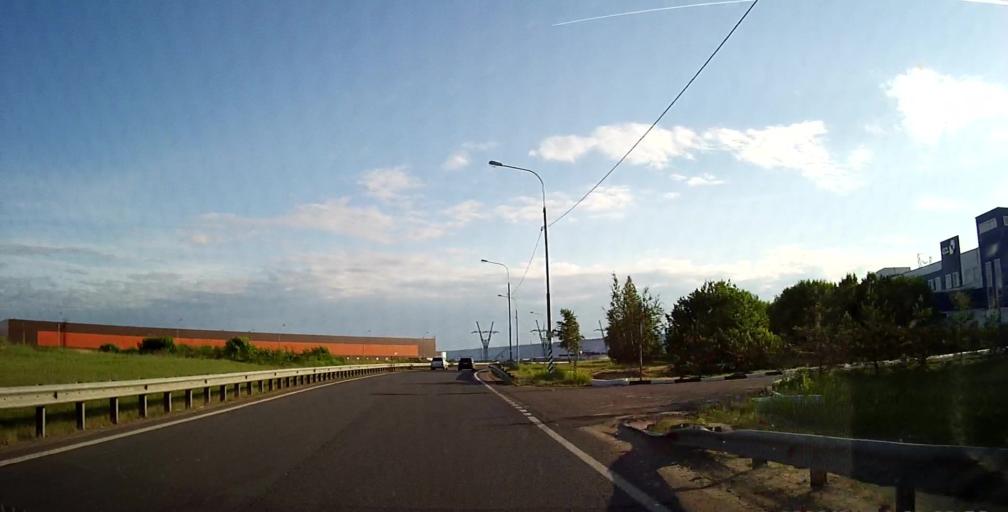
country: RU
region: Moskovskaya
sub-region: Podol'skiy Rayon
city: Podol'sk
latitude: 55.4376
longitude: 37.6106
